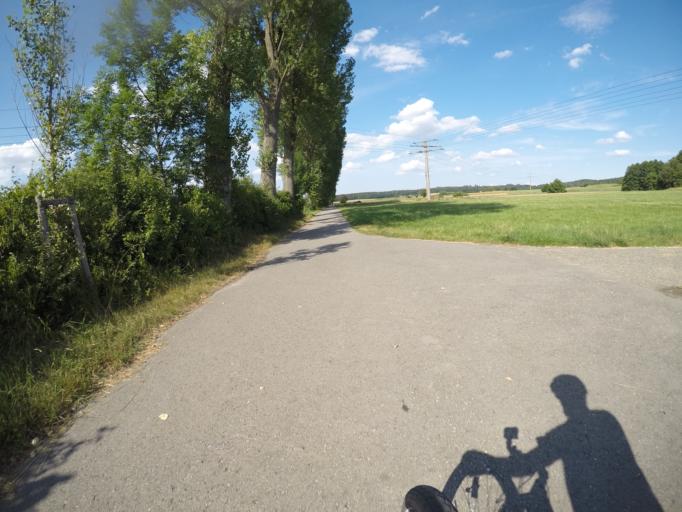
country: DE
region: Baden-Wuerttemberg
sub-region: Regierungsbezirk Stuttgart
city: Gartringen
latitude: 48.6306
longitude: 8.9267
